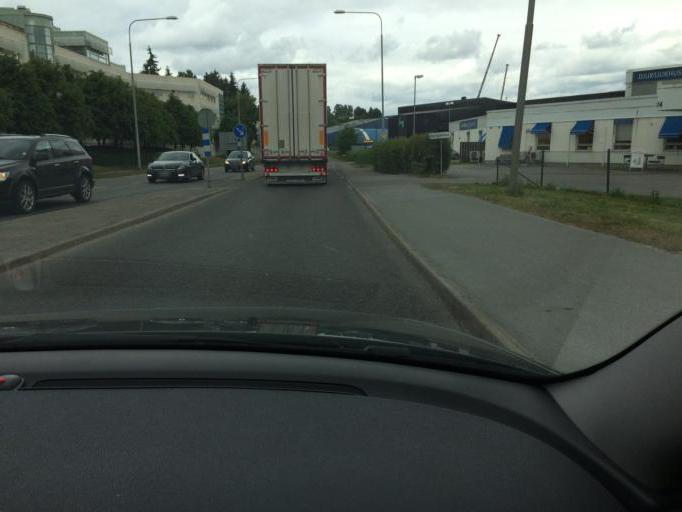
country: SE
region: Stockholm
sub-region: Stockholms Kommun
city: Kista
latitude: 59.3788
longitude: 17.9053
